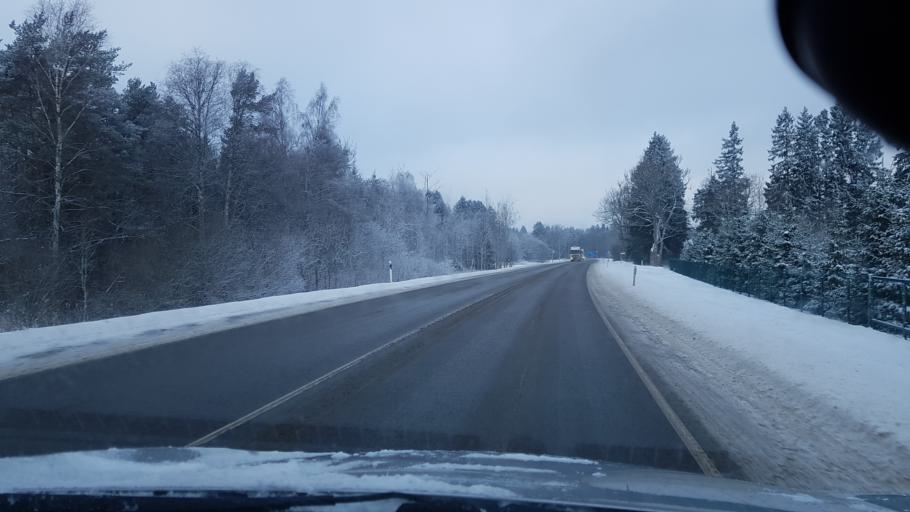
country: EE
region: Harju
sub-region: Keila linn
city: Keila
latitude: 59.3382
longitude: 24.2735
